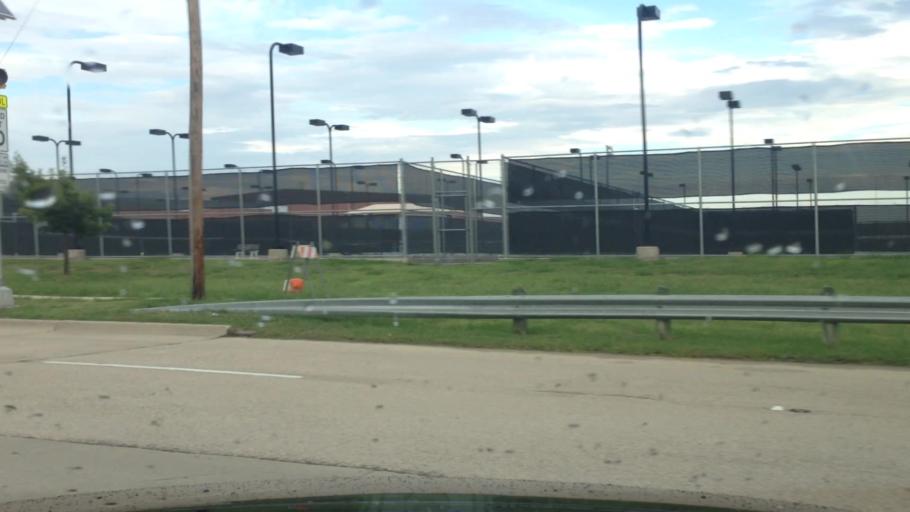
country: US
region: Texas
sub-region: Denton County
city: Lewisville
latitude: 33.0059
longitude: -97.0278
